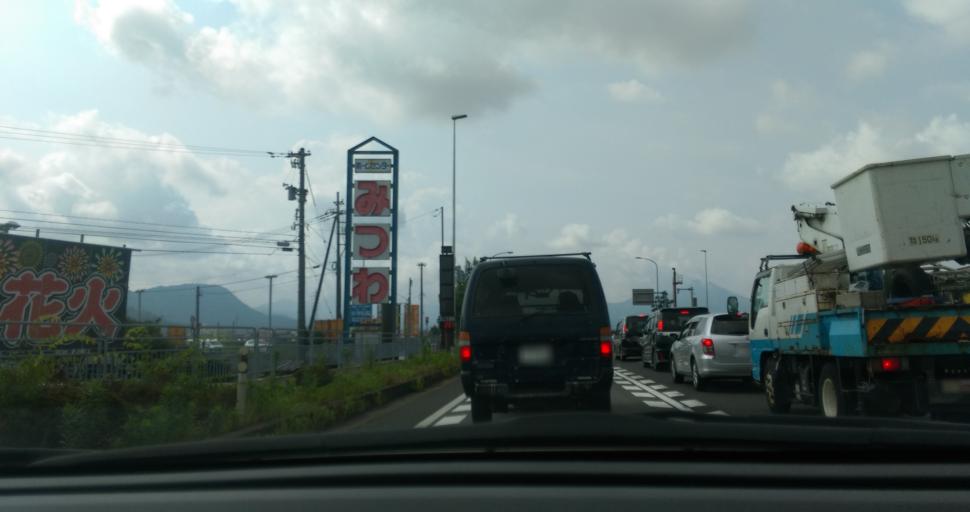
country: JP
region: Fukui
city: Sabae
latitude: 35.9565
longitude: 136.1887
